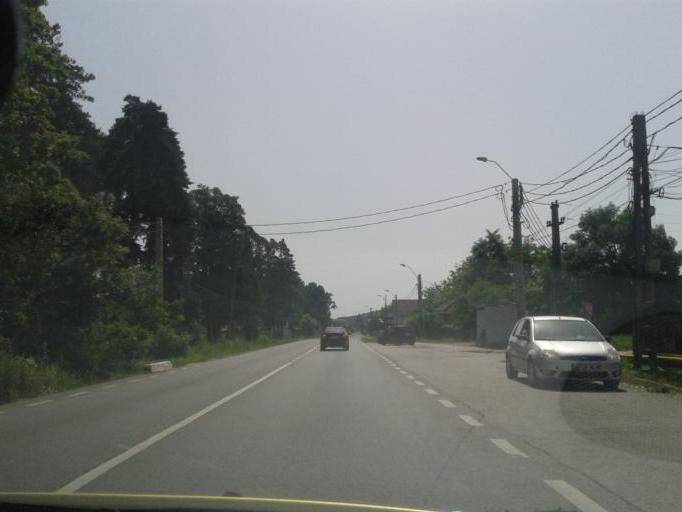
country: RO
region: Arges
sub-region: Comuna Bascov
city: Bascov
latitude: 44.8874
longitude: 24.7761
